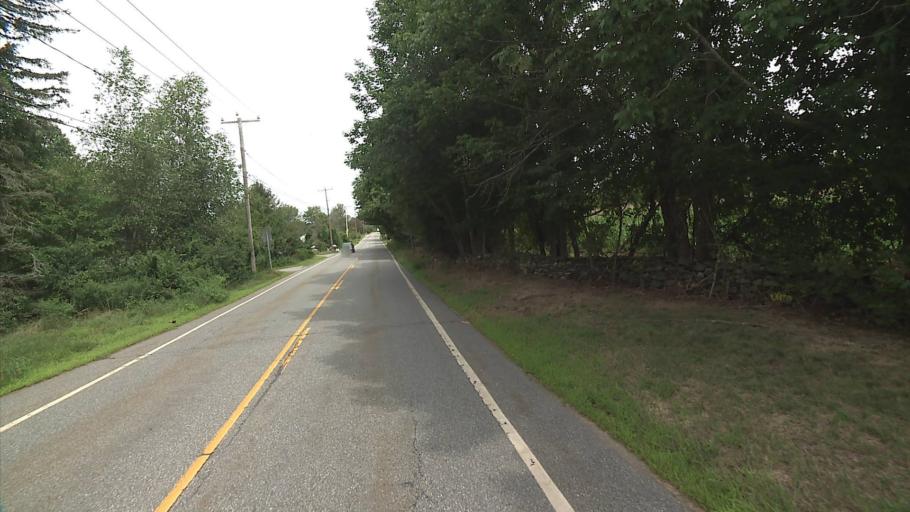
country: US
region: Connecticut
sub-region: Windham County
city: Thompson
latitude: 41.9950
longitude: -71.8443
